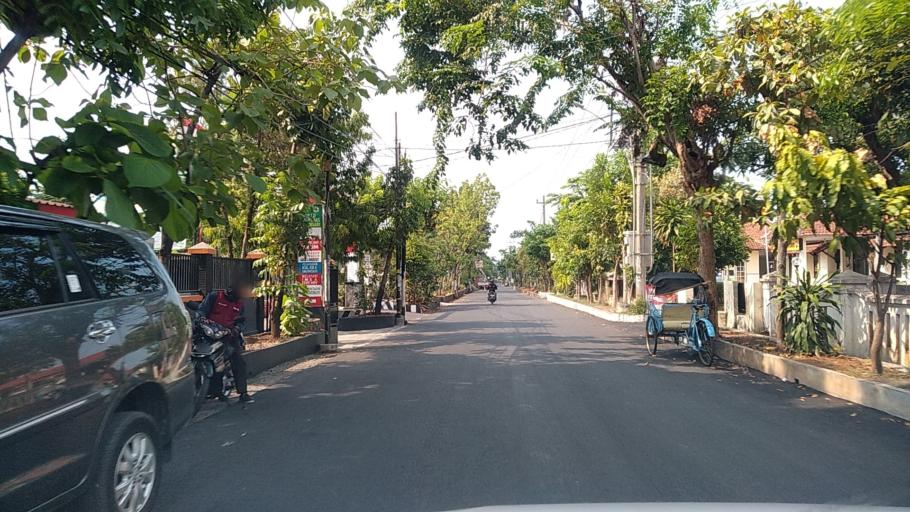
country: ID
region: Central Java
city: Semarang
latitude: -7.0001
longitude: 110.4490
